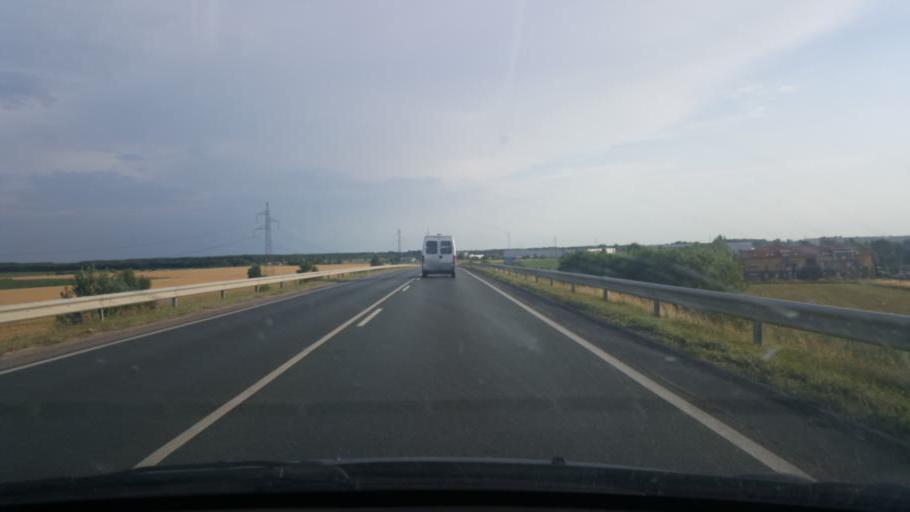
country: HU
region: Pest
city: Ullo
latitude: 47.3843
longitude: 19.3657
